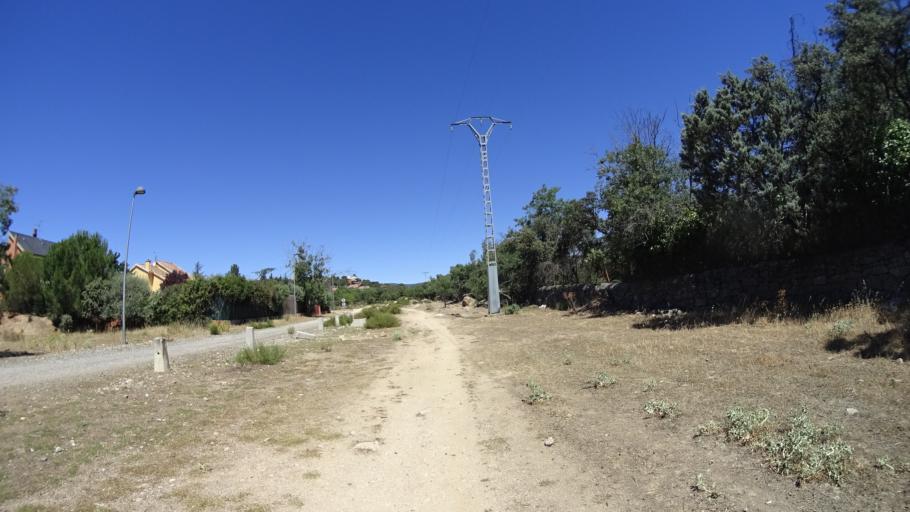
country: ES
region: Madrid
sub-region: Provincia de Madrid
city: Alpedrete
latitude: 40.6531
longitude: -4.0436
